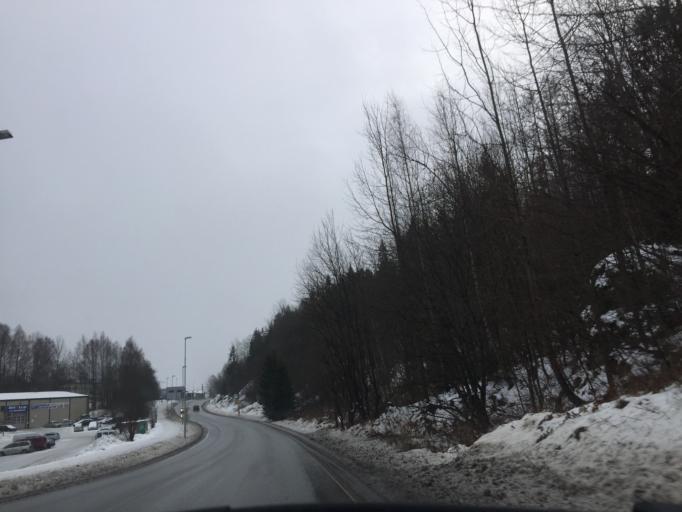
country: NO
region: Akershus
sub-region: Frogn
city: Drobak
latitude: 59.6724
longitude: 10.6580
